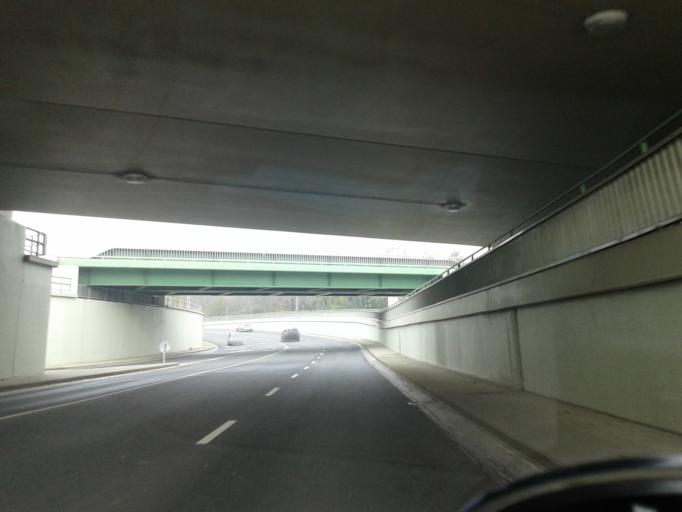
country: HU
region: Budapest
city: Budapest XXII. keruelet
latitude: 47.4014
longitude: 19.0144
